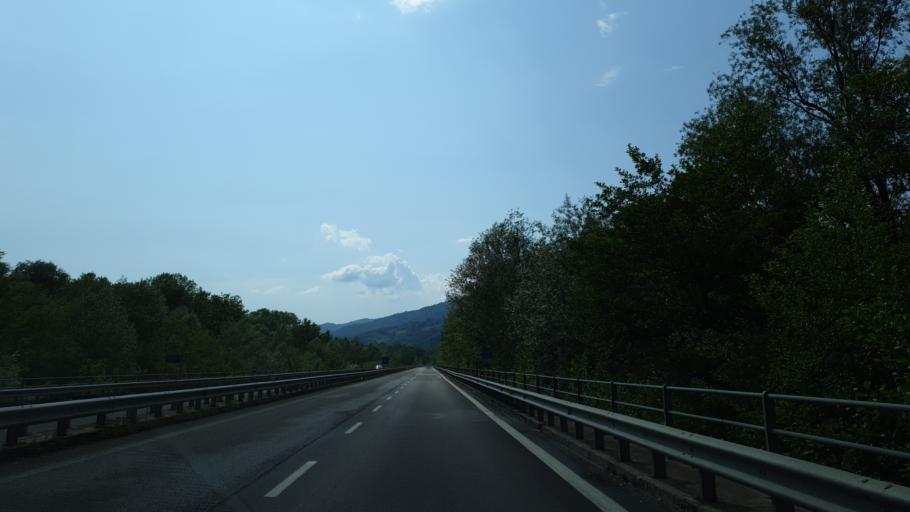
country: IT
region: Emilia-Romagna
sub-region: Forli-Cesena
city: Sarsina
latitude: 43.8887
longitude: 12.0620
